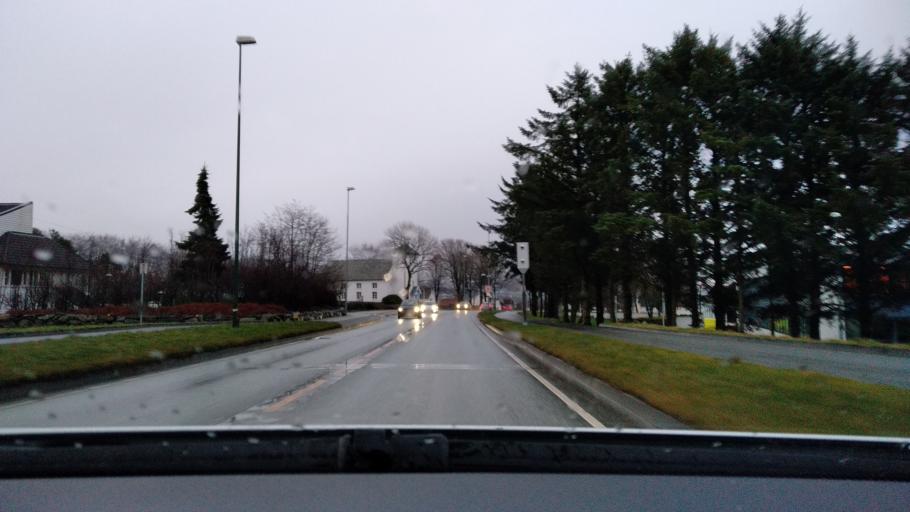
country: NO
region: Rogaland
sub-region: Randaberg
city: Randaberg
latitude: 58.9529
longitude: 5.6417
